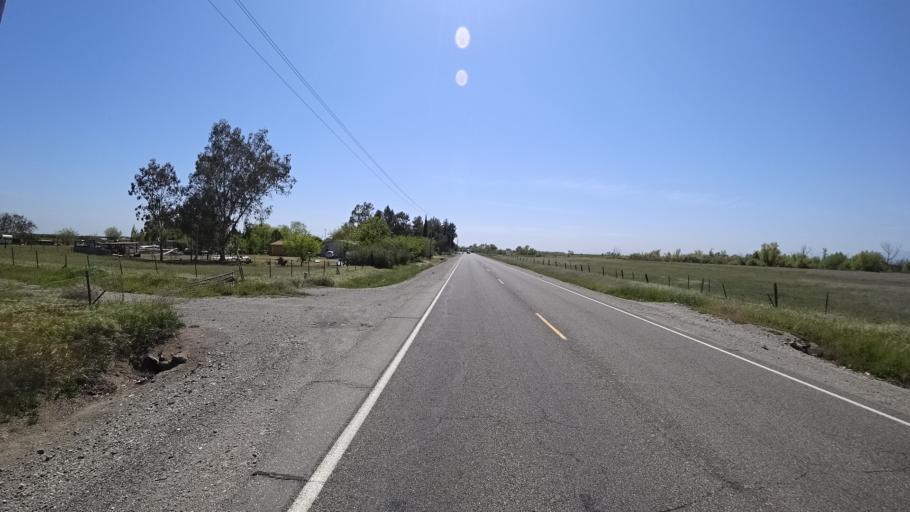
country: US
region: California
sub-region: Glenn County
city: Willows
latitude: 39.6313
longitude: -122.1975
